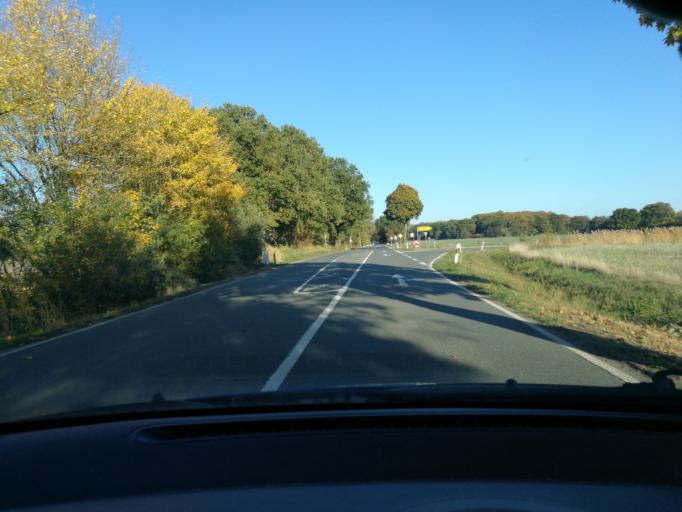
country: DE
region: Lower Saxony
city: Hittbergen
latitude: 53.3302
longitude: 10.5933
